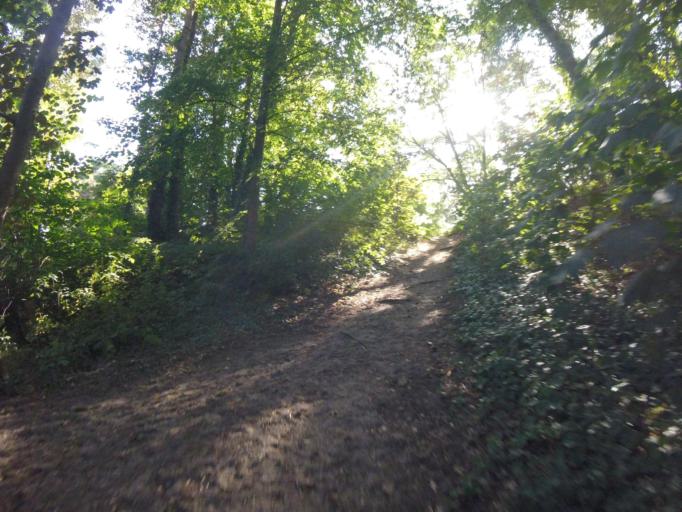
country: DE
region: Brandenburg
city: Wildau
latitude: 52.3121
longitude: 13.7052
